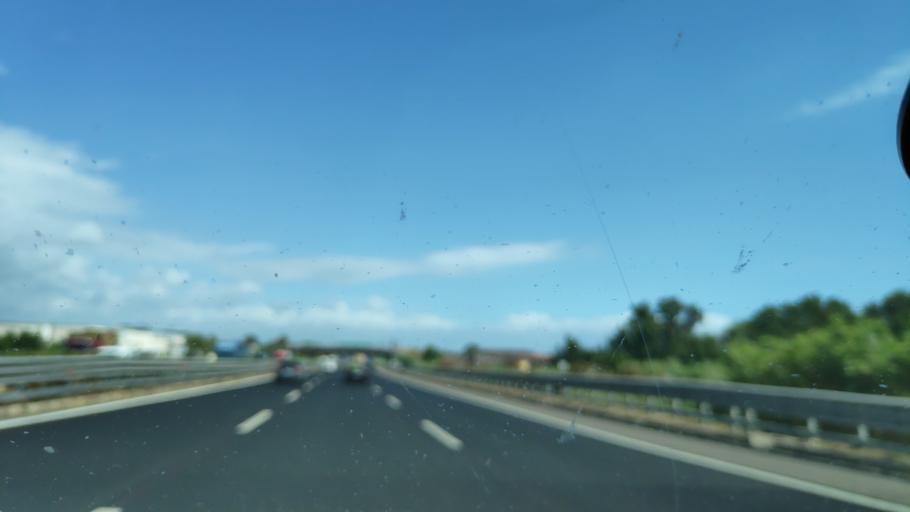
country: IT
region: Campania
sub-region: Provincia di Salerno
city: Pontecagnano
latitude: 40.6531
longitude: 14.8722
